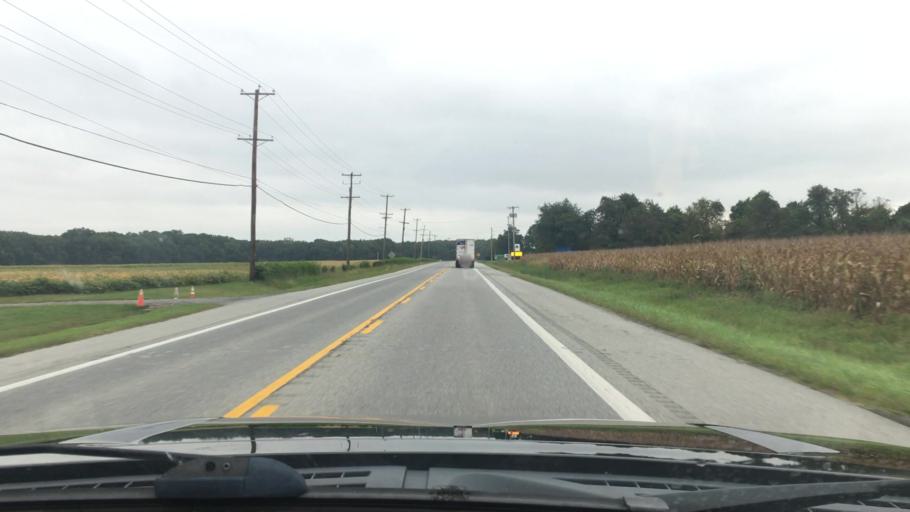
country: US
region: Maryland
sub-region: Cecil County
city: Elkton
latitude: 39.4910
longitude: -75.8442
